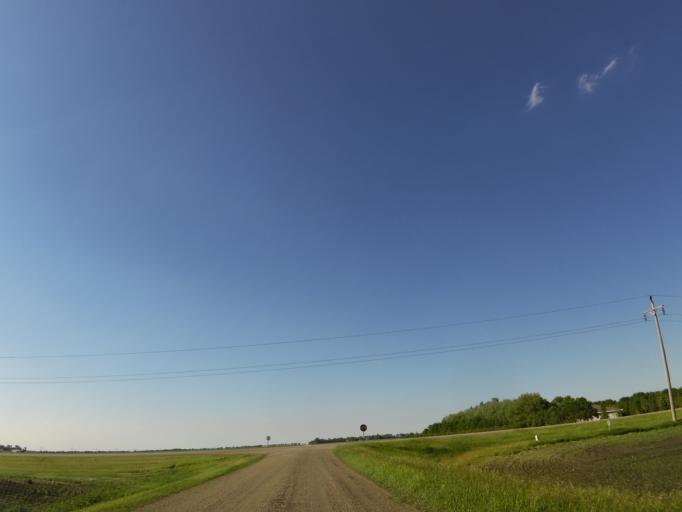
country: US
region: North Dakota
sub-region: Walsh County
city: Grafton
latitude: 48.4111
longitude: -97.2564
